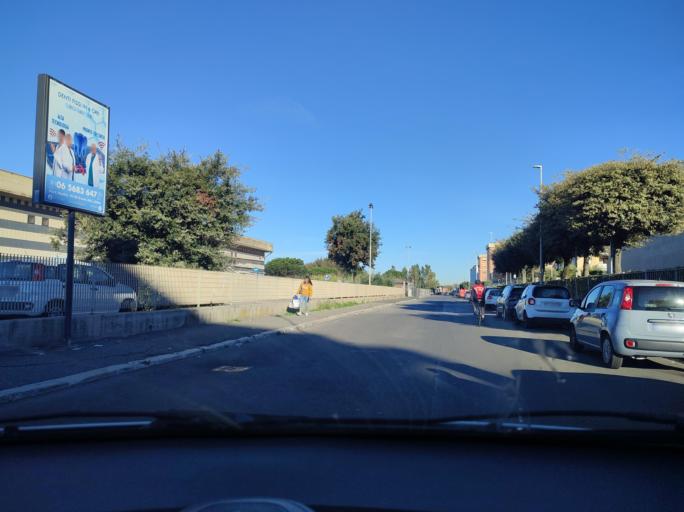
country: IT
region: Latium
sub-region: Citta metropolitana di Roma Capitale
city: Lido di Ostia
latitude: 41.7404
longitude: 12.2647
